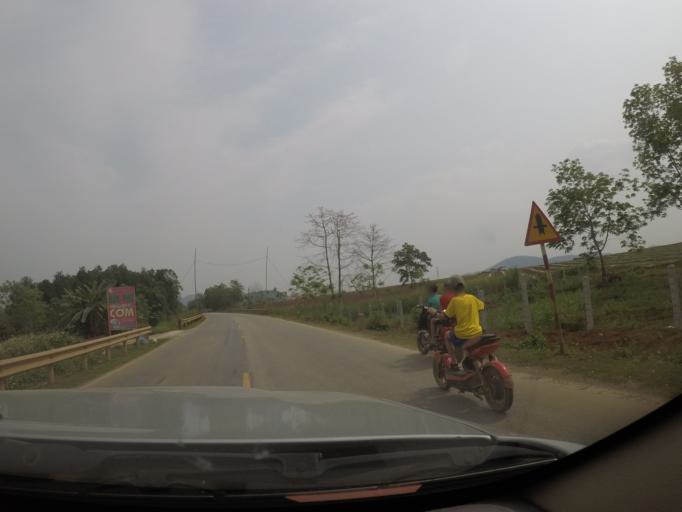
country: VN
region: Nghe An
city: Cau Giat
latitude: 19.3597
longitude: 105.4660
